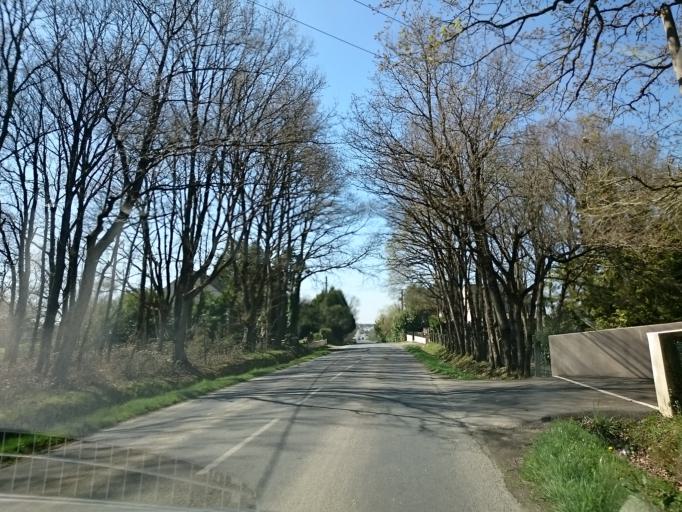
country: FR
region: Brittany
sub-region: Departement d'Ille-et-Vilaine
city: Orgeres
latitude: 48.0046
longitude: -1.6844
